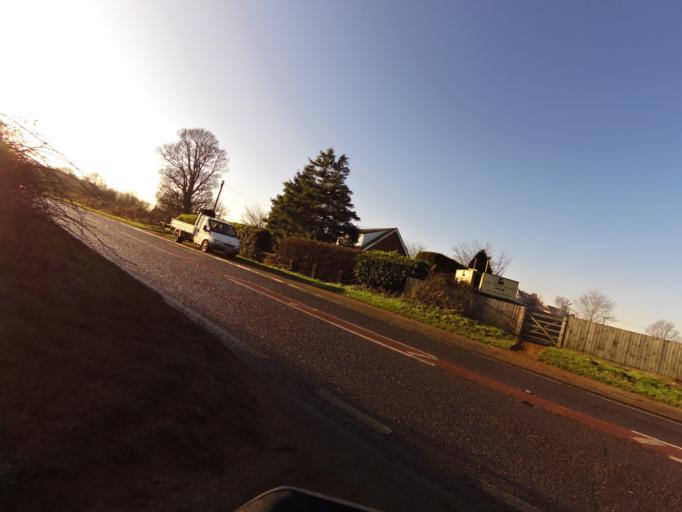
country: GB
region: England
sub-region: Norfolk
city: Aylsham
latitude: 52.7886
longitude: 1.2644
